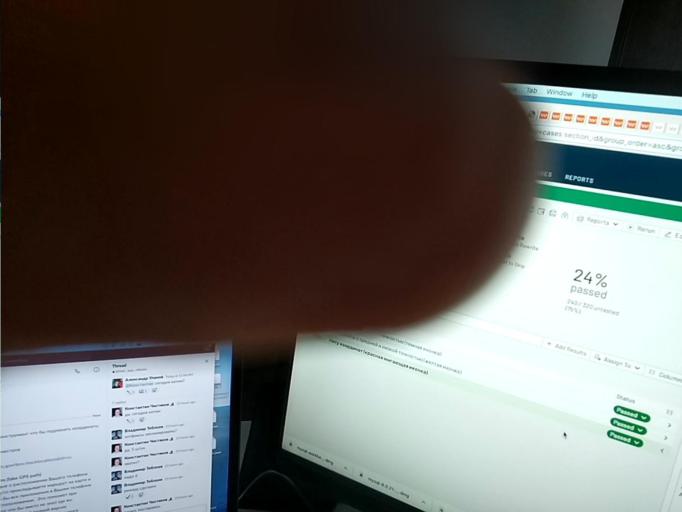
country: AM
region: Yerevan
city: Yerevan
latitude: 40.2010
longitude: 44.4987
